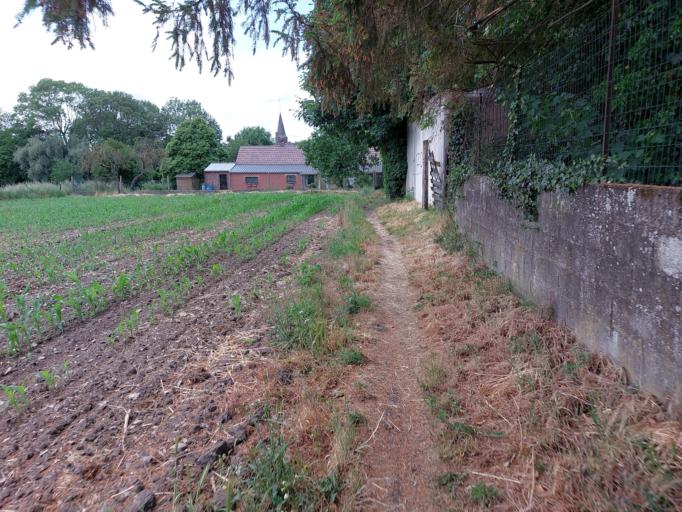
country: BE
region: Wallonia
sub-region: Province du Hainaut
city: Saint-Ghislain
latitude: 50.4861
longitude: 3.7934
